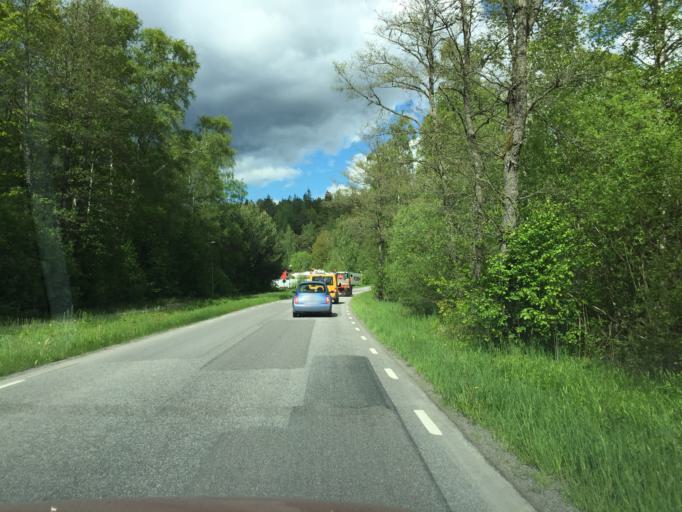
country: SE
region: OEstergoetland
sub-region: Finspangs Kommun
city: Finspang
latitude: 58.7151
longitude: 15.8320
